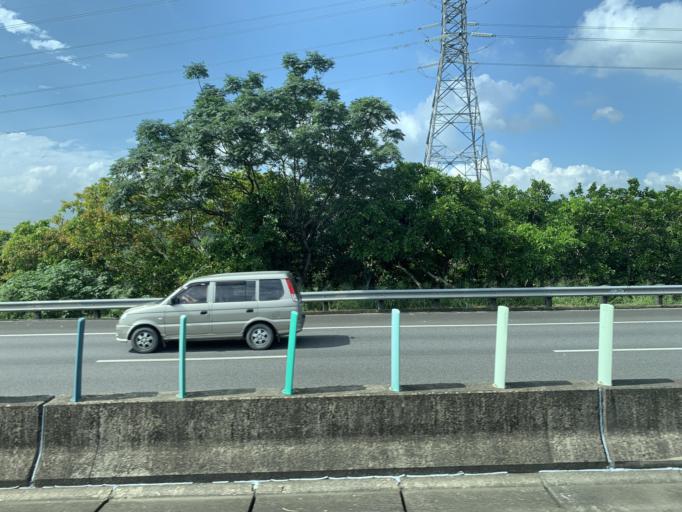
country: TW
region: Taiwan
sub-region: Pingtung
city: Pingtung
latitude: 22.8586
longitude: 120.4932
